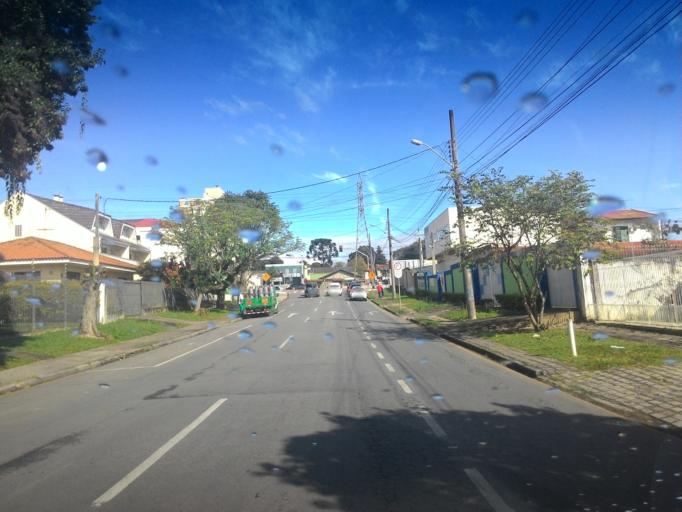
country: BR
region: Parana
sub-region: Curitiba
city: Curitiba
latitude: -25.4568
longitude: -49.2392
